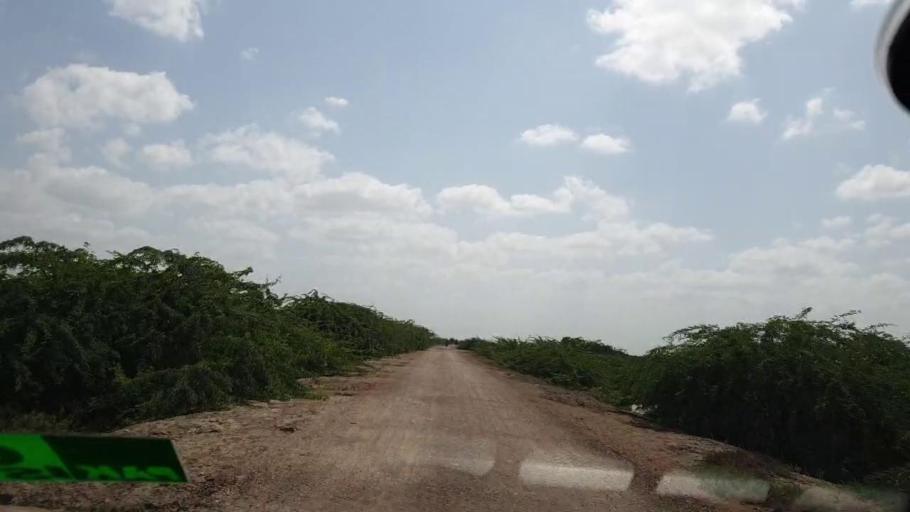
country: PK
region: Sindh
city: Kadhan
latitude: 24.5938
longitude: 69.1832
